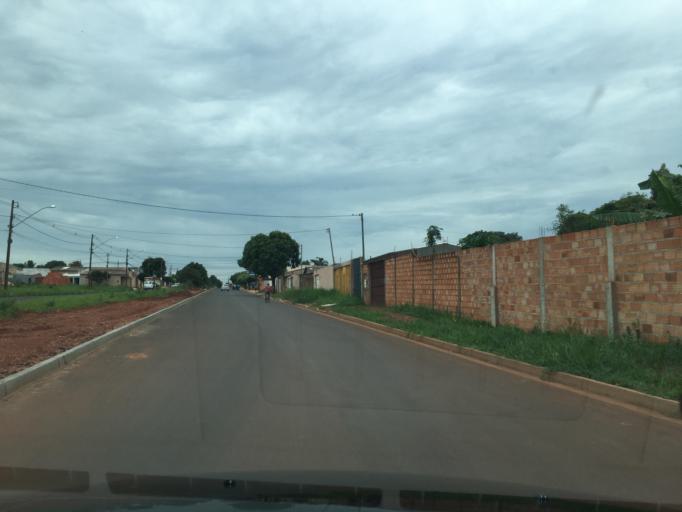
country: BR
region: Minas Gerais
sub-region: Uberlandia
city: Uberlandia
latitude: -18.8683
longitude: -48.2240
